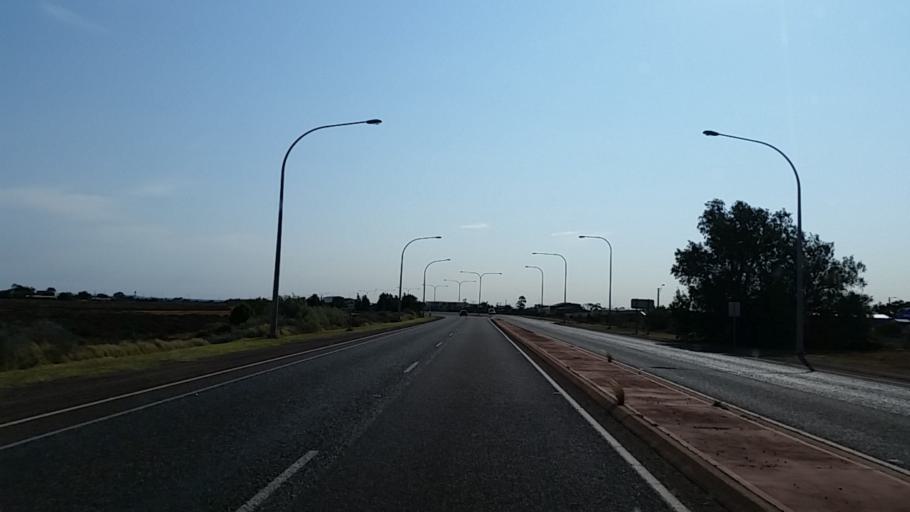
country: AU
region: South Australia
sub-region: Whyalla
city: Whyalla
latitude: -33.0400
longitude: 137.5582
